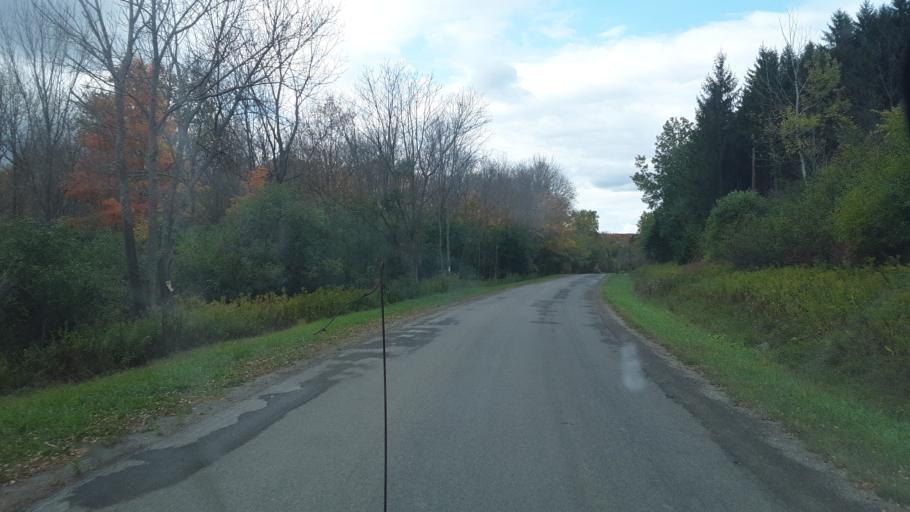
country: US
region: New York
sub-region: Allegany County
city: Alfred
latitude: 42.3645
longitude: -77.8344
